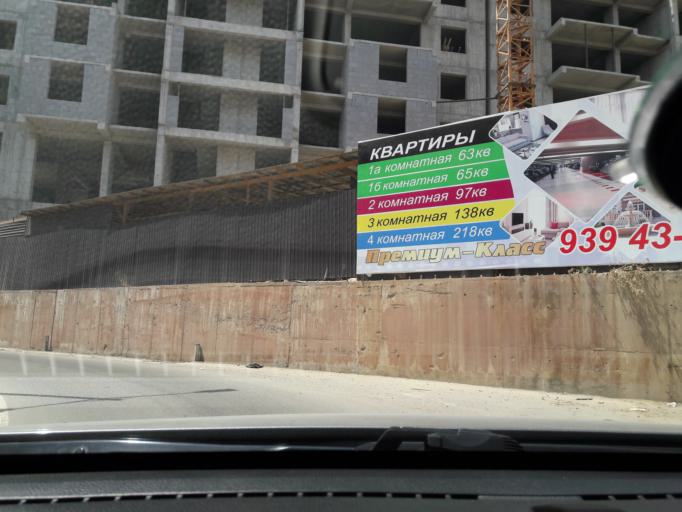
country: TJ
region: Dushanbe
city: Dushanbe
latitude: 38.5749
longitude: 68.8009
